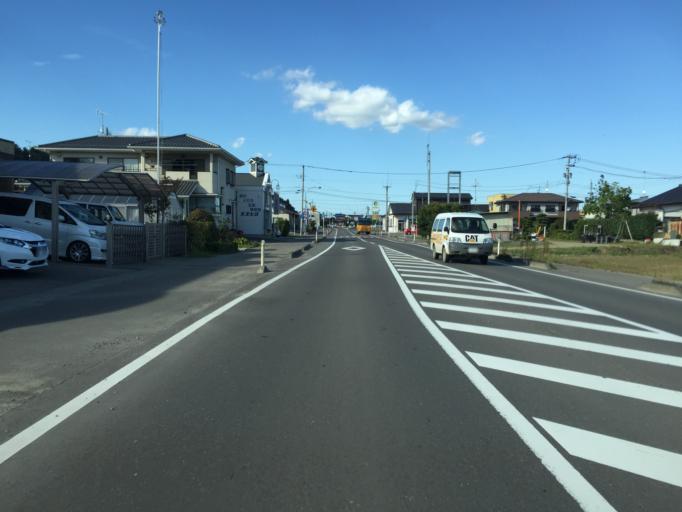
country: JP
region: Miyagi
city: Marumori
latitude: 37.9110
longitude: 140.7641
